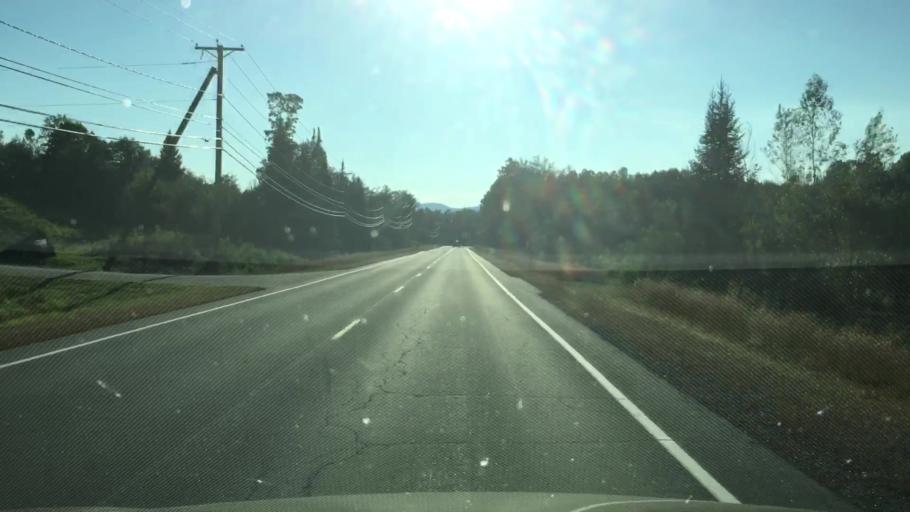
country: US
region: New Hampshire
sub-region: Grafton County
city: Littleton
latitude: 44.3095
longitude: -71.8446
